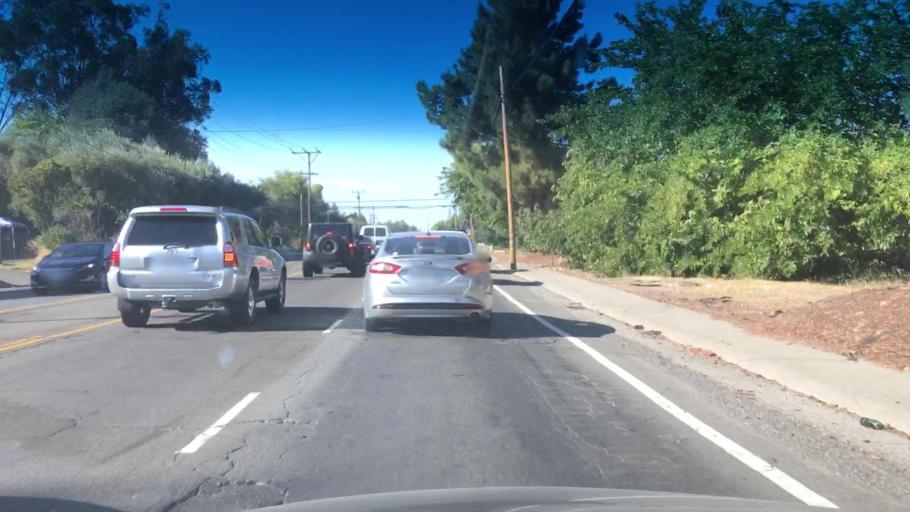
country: US
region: California
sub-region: Sacramento County
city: Orangevale
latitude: 38.6594
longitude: -121.2256
